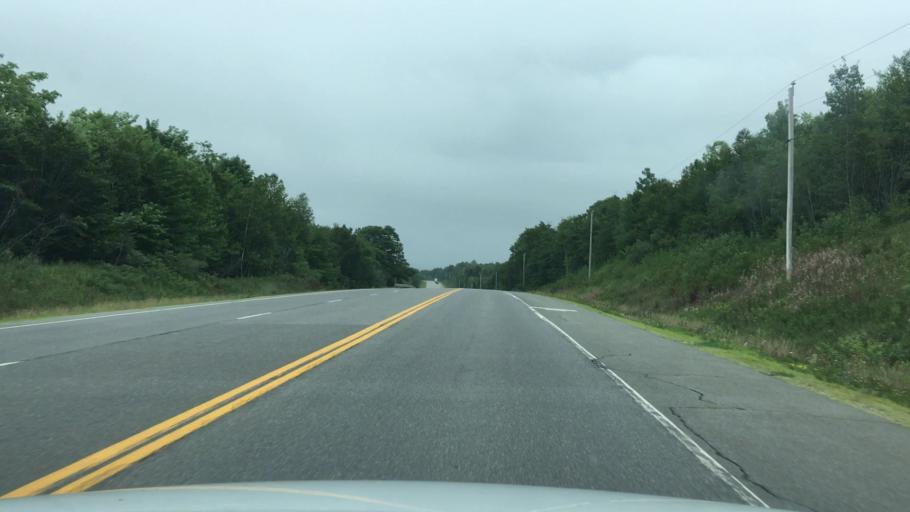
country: US
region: Maine
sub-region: Hancock County
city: Franklin
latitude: 44.8273
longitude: -68.1211
